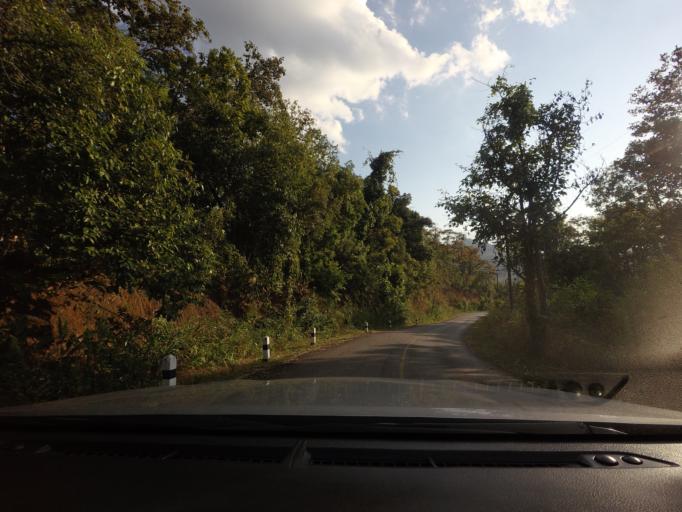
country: TH
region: Chiang Mai
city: Phrao
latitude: 19.5027
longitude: 99.1692
